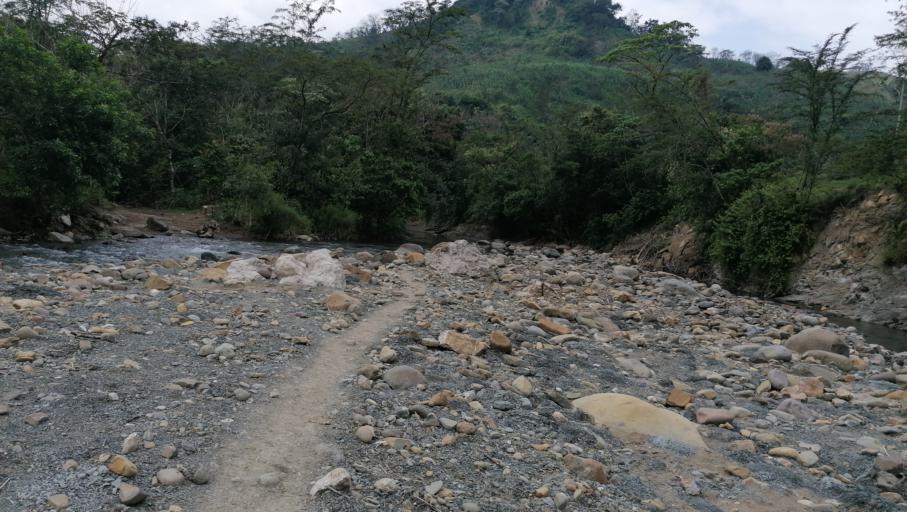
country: MX
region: Chiapas
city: Ocotepec
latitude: 17.2978
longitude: -93.2278
